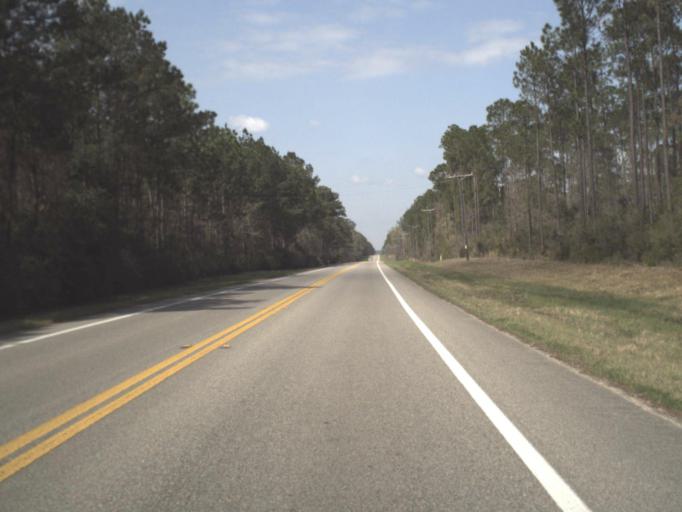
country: US
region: Florida
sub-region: Liberty County
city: Bristol
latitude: 30.3836
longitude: -84.7400
